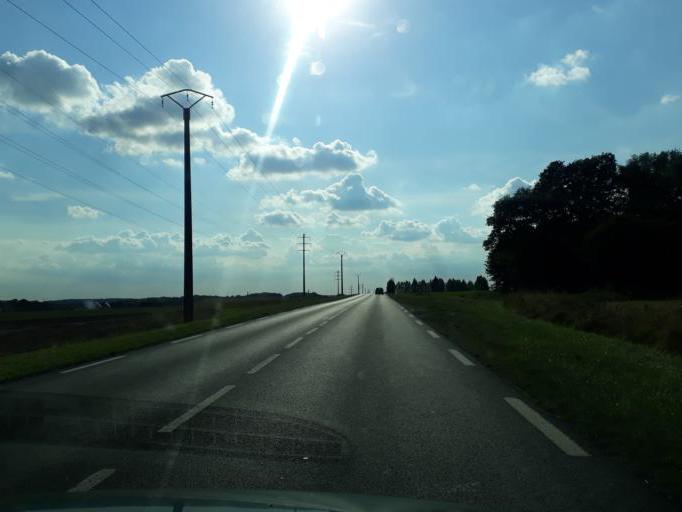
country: FR
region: Centre
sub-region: Departement du Loir-et-Cher
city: Moree
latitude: 47.9042
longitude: 1.2802
